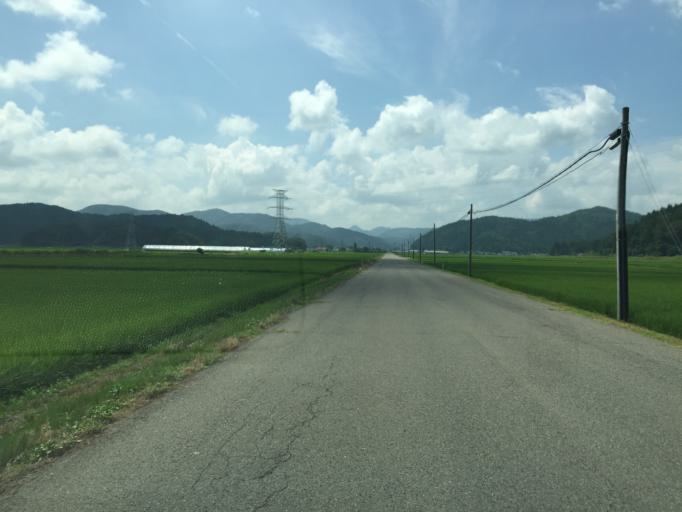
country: JP
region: Fukushima
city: Inawashiro
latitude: 37.4066
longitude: 140.0857
